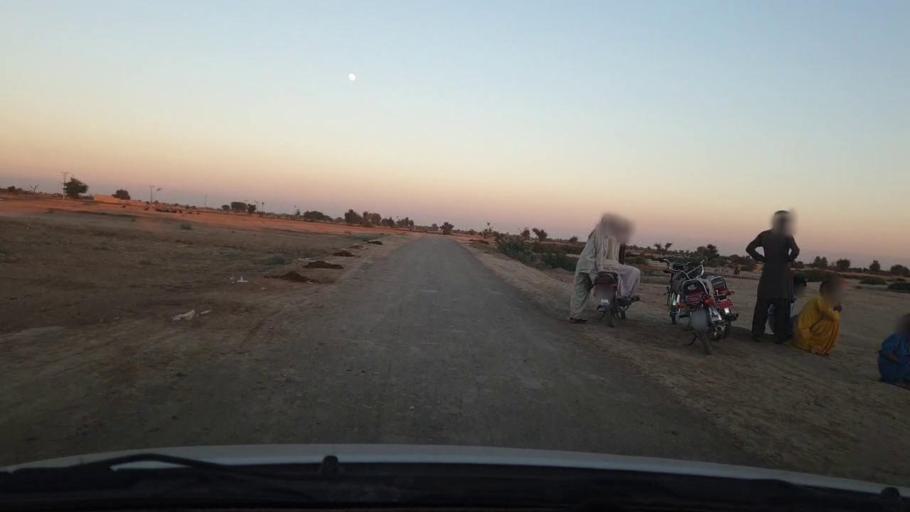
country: PK
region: Sindh
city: Johi
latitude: 26.8296
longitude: 67.4469
